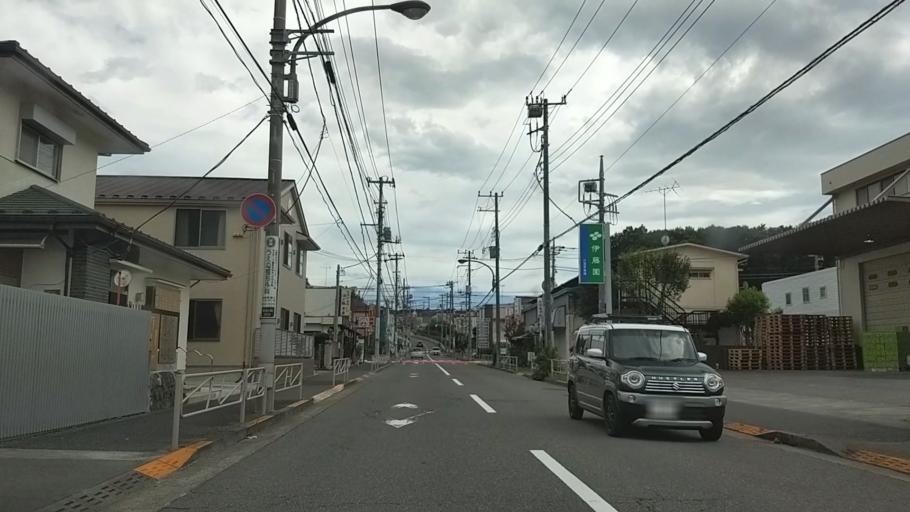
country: JP
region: Tokyo
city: Hachioji
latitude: 35.6455
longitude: 139.2979
